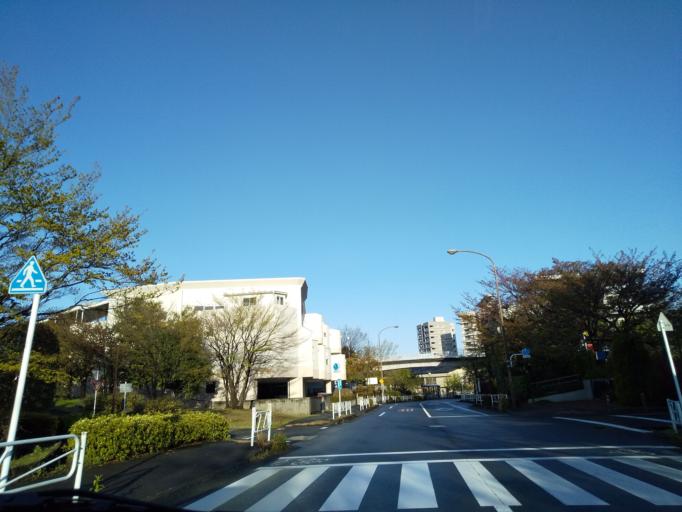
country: JP
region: Tokyo
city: Hachioji
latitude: 35.6162
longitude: 139.3713
